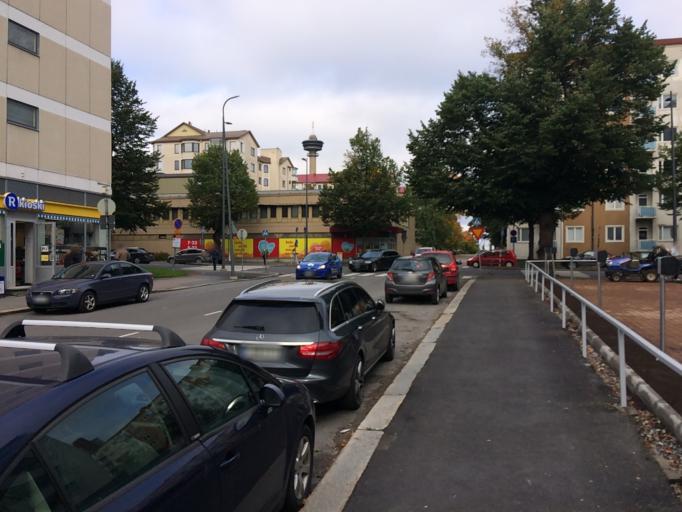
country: FI
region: Pirkanmaa
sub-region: Tampere
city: Tampere
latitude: 61.4996
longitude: 23.7490
